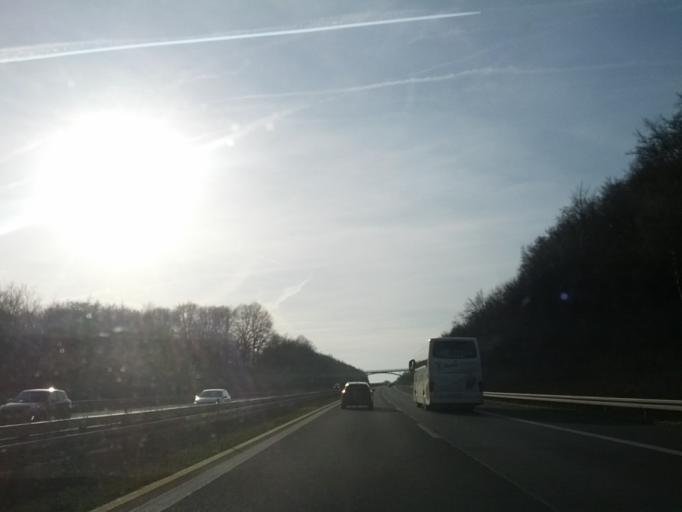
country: DE
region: Bavaria
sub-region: Regierungsbezirk Unterfranken
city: Unterpleichfeld
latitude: 49.8882
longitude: 9.9991
